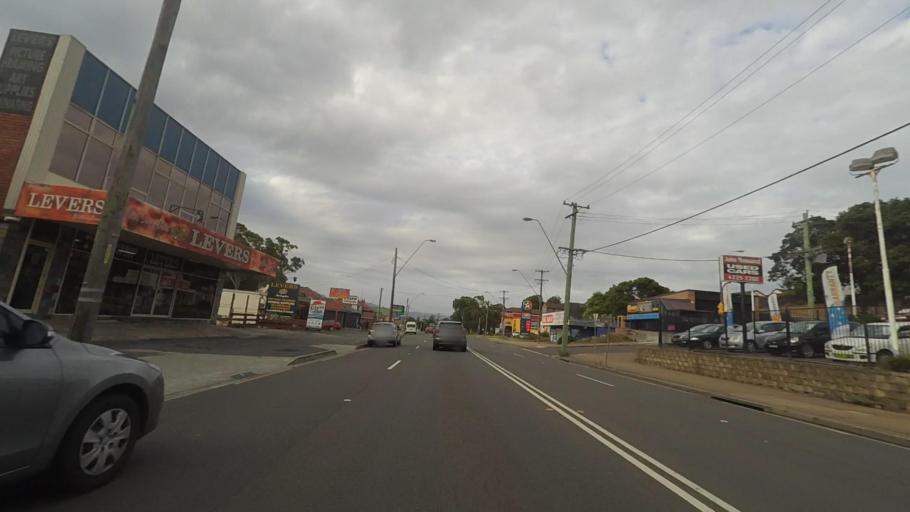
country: AU
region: New South Wales
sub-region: Wollongong
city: Gwynneville
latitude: -34.4160
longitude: 150.8927
